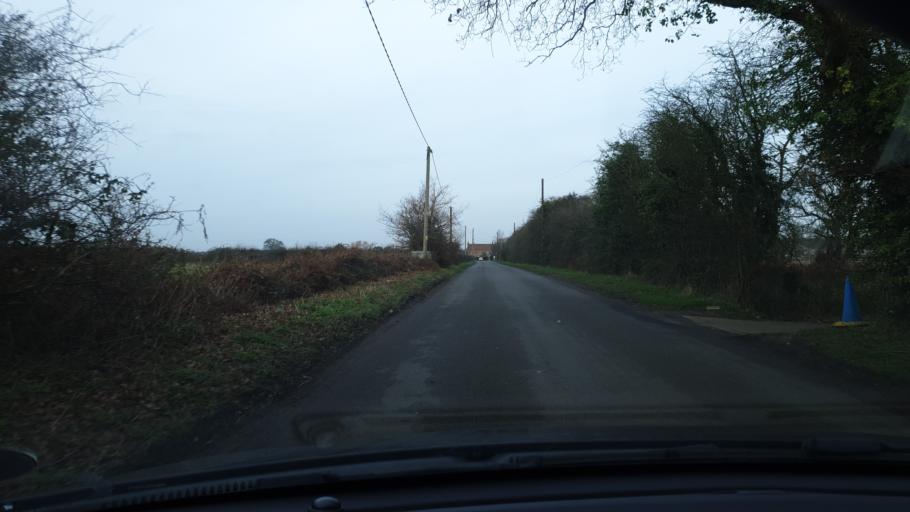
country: GB
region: England
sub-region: Essex
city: Saint Osyth
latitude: 51.8212
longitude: 1.0990
